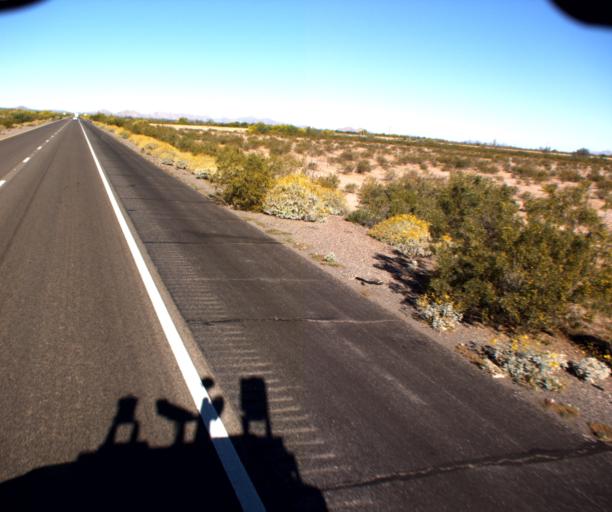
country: US
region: Arizona
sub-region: Pinal County
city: Casa Grande
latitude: 32.8287
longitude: -111.9762
